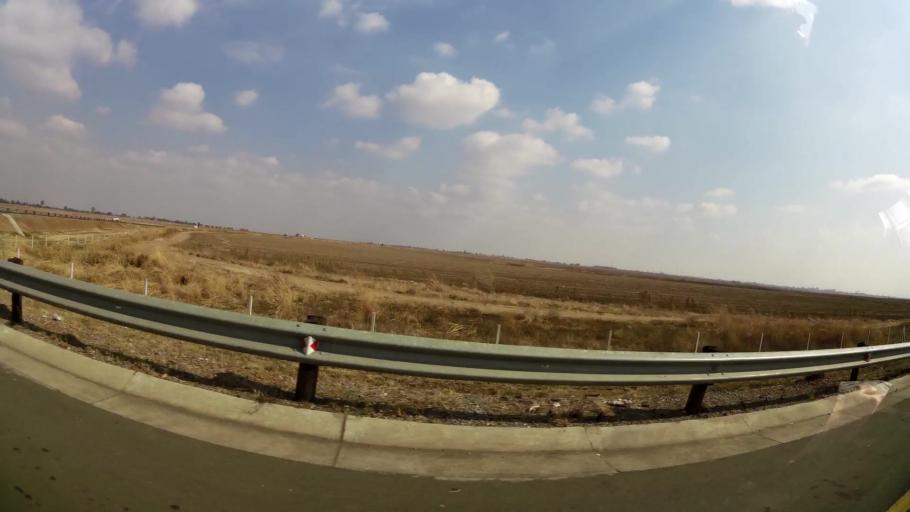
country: ZA
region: Gauteng
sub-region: Ekurhuleni Metropolitan Municipality
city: Springs
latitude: -26.1597
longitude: 28.4441
